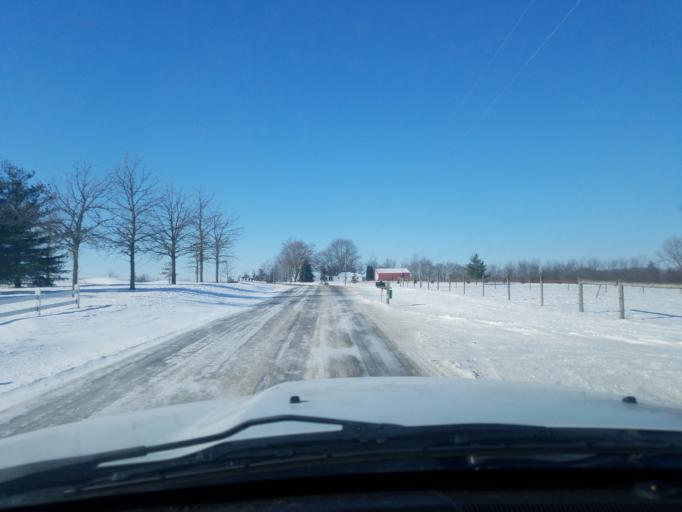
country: US
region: Indiana
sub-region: Noble County
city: Kendallville
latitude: 41.4125
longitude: -85.2430
